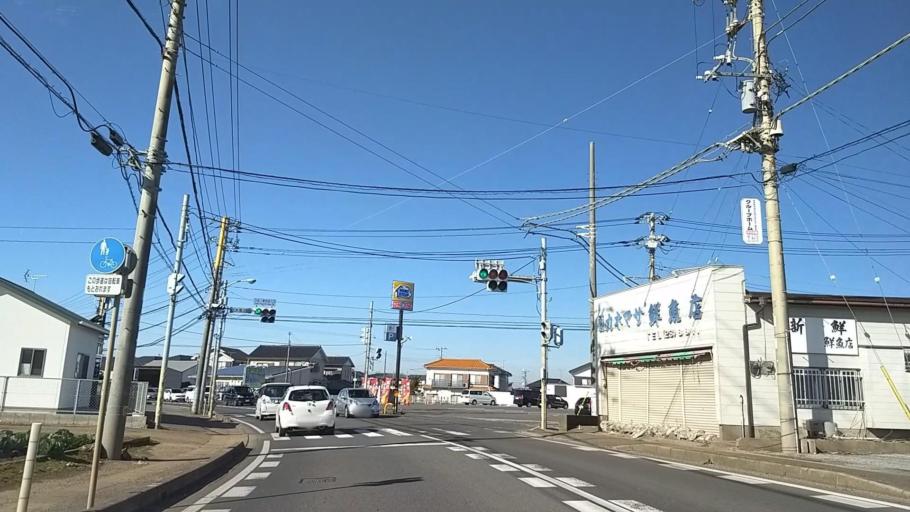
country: JP
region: Chiba
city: Hasaki
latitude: 35.7142
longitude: 140.7724
